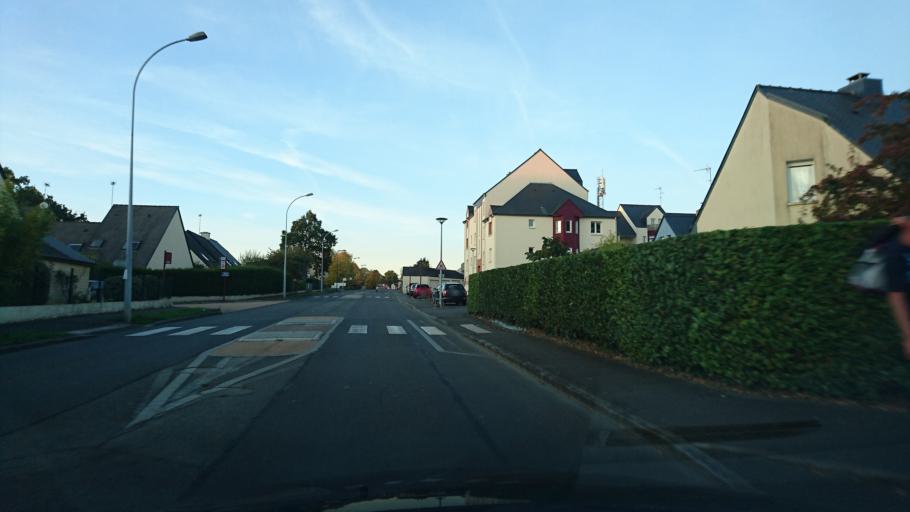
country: FR
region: Brittany
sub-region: Departement d'Ille-et-Vilaine
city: Bruz
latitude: 48.0229
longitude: -1.7527
